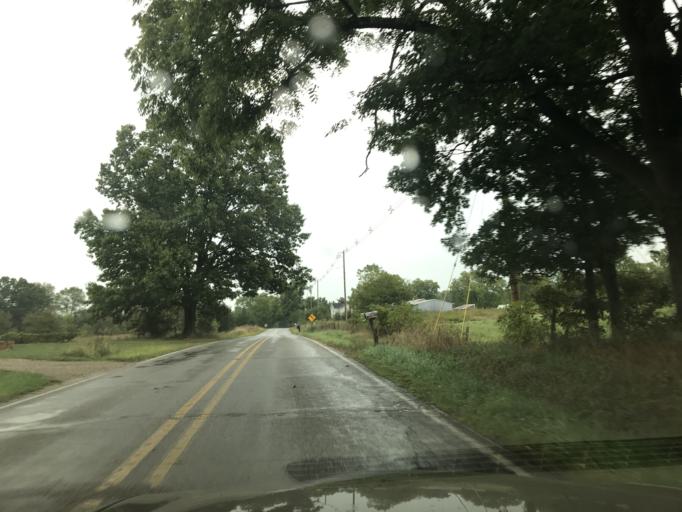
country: US
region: Michigan
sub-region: Ingham County
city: Leslie
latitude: 42.3648
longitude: -84.5477
